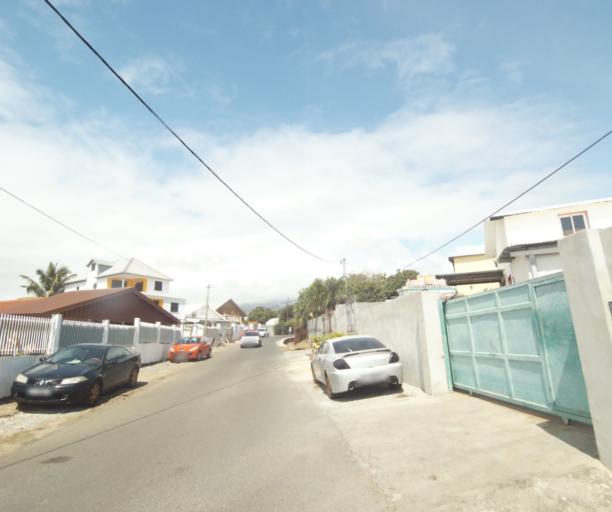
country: RE
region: Reunion
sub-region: Reunion
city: Saint-Paul
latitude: -21.0547
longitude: 55.2587
